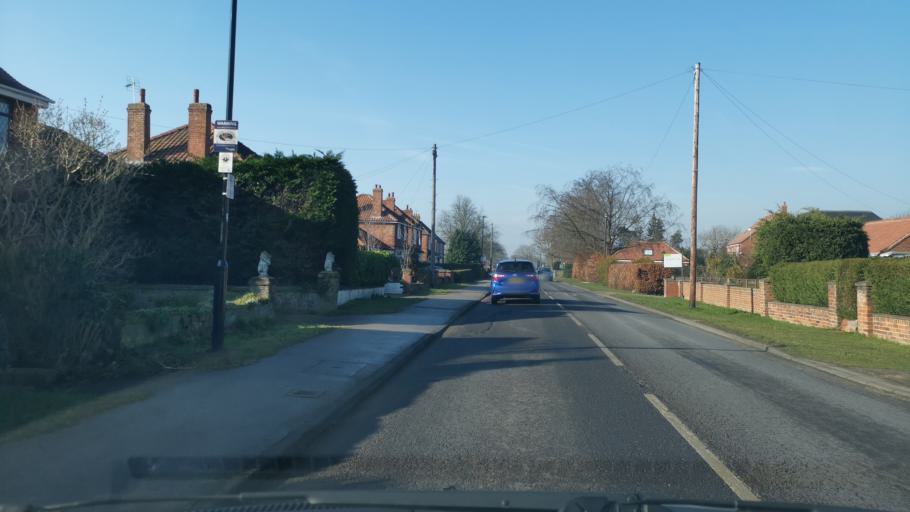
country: GB
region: England
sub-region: City of York
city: Murton
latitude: 53.9874
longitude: -1.0252
